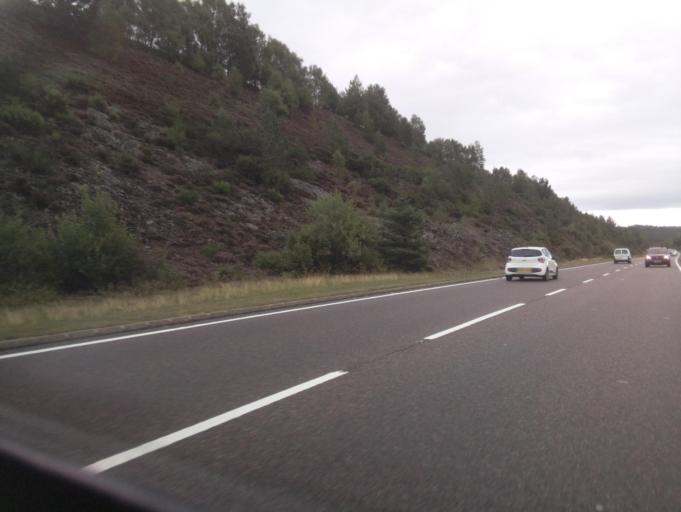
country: GB
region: Scotland
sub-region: Highland
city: Aviemore
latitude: 57.3003
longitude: -3.9249
